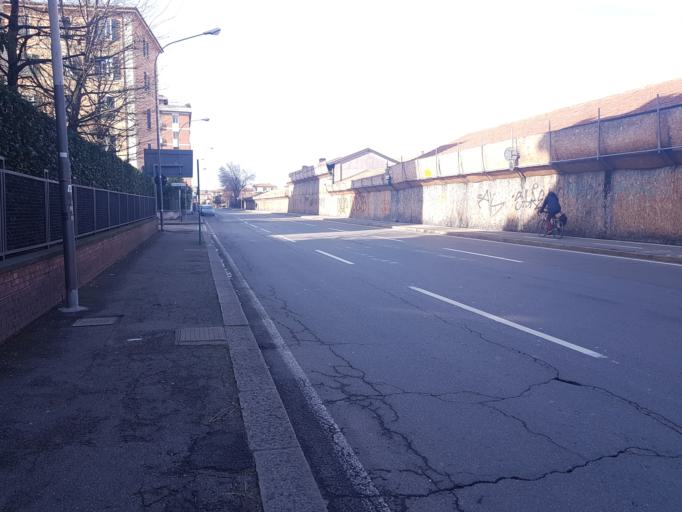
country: IT
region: Emilia-Romagna
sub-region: Provincia di Bologna
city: Bologna
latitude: 44.4969
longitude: 11.3265
